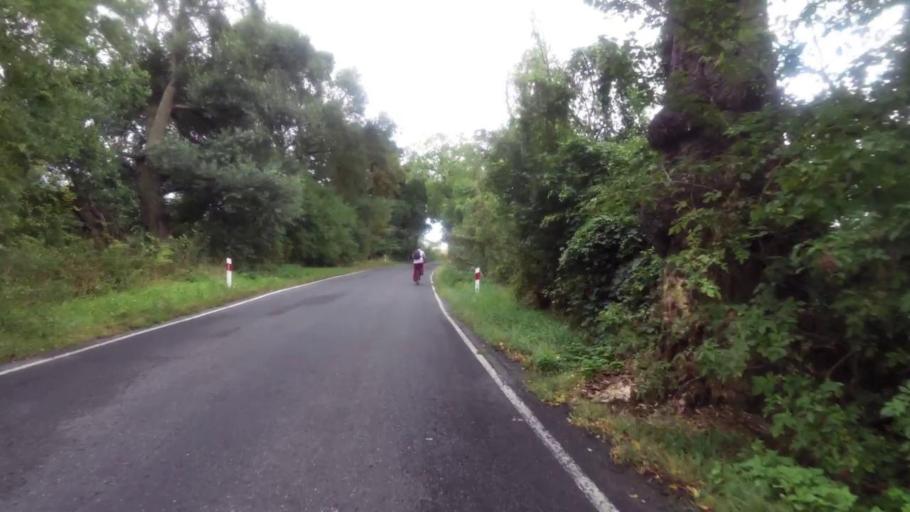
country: PL
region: West Pomeranian Voivodeship
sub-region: Powiat mysliborski
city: Debno
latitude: 52.6878
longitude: 14.6462
